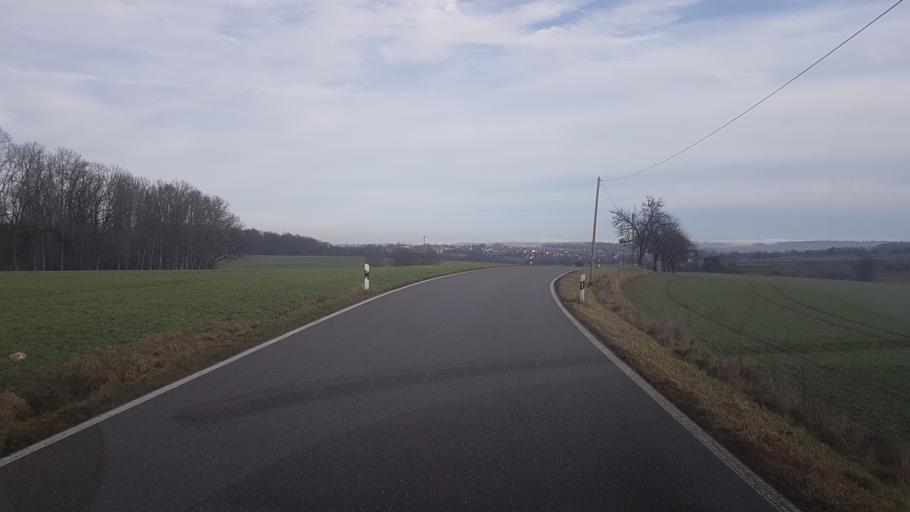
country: DE
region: Baden-Wuerttemberg
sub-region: Regierungsbezirk Stuttgart
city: Wallhausen
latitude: 49.2086
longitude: 10.0413
